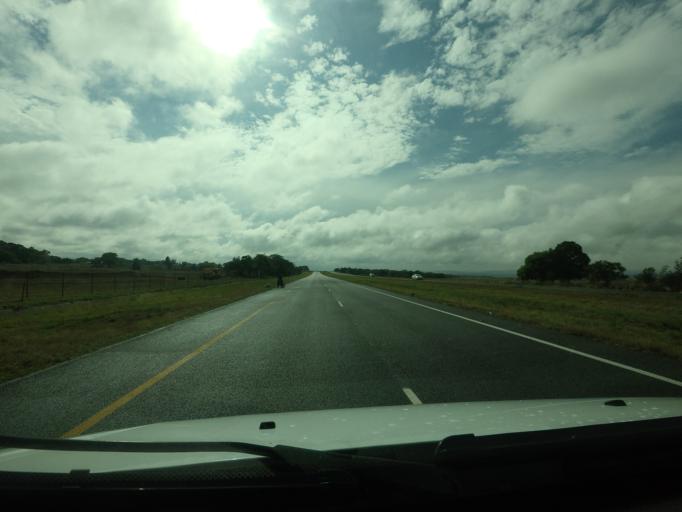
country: ZA
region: Gauteng
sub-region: City of Tshwane Metropolitan Municipality
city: Cullinan
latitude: -25.7984
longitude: 28.5802
